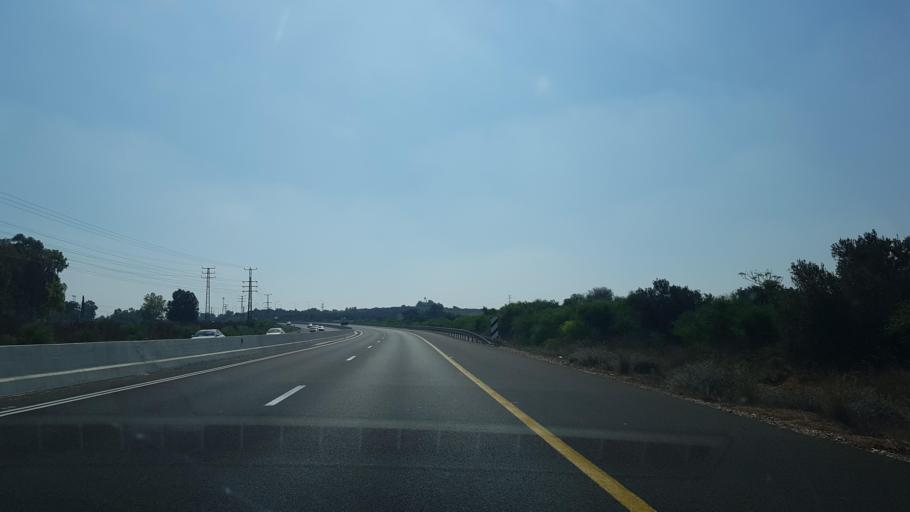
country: IL
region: Southern District
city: Ashqelon
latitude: 31.6888
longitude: 34.6713
